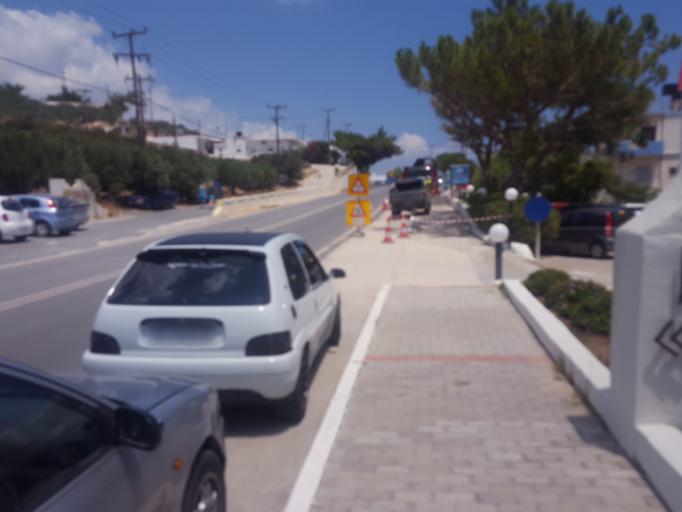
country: GR
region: Crete
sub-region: Nomos Lasithiou
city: Kato Chorio
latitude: 35.0124
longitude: 25.8371
